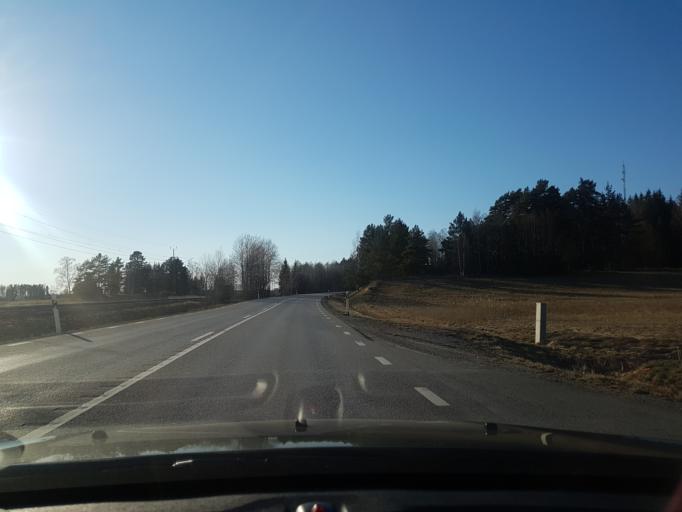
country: SE
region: Uppsala
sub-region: Heby Kommun
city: Morgongava
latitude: 59.9095
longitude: 17.0358
